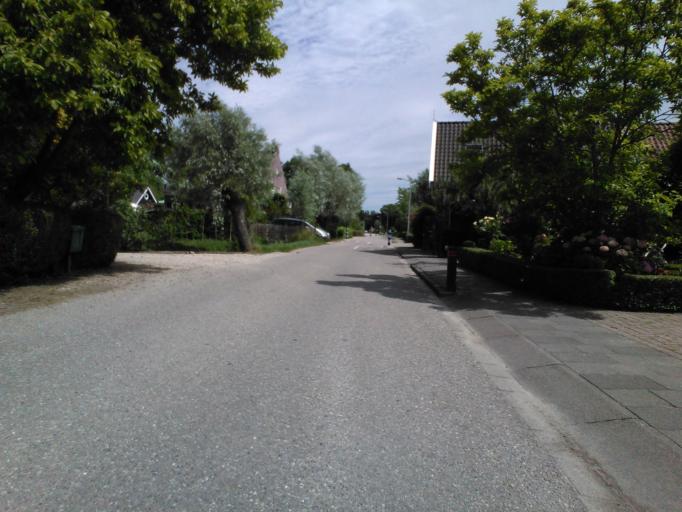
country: NL
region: South Holland
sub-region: Gemeente Sliedrecht
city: Sliedrecht
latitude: 51.8447
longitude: 4.7645
